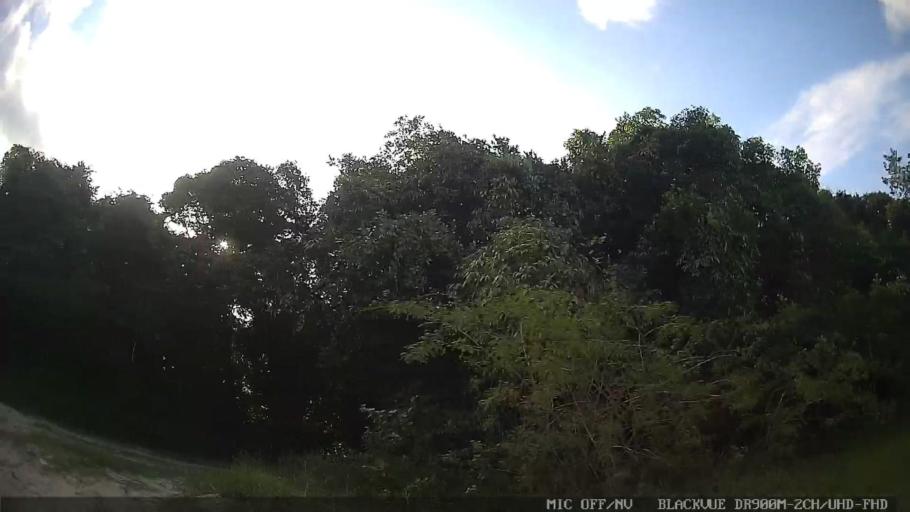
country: BR
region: Sao Paulo
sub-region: Itanhaem
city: Itanhaem
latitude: -24.1488
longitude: -46.8132
